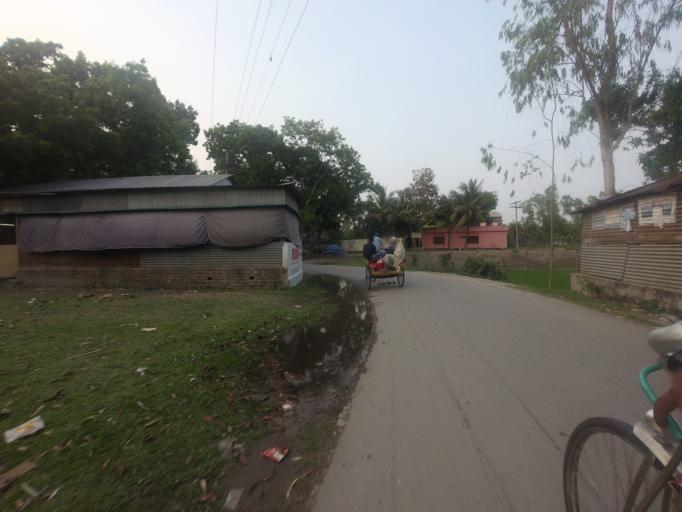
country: BD
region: Rajshahi
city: Sirajganj
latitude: 24.3309
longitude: 89.6918
